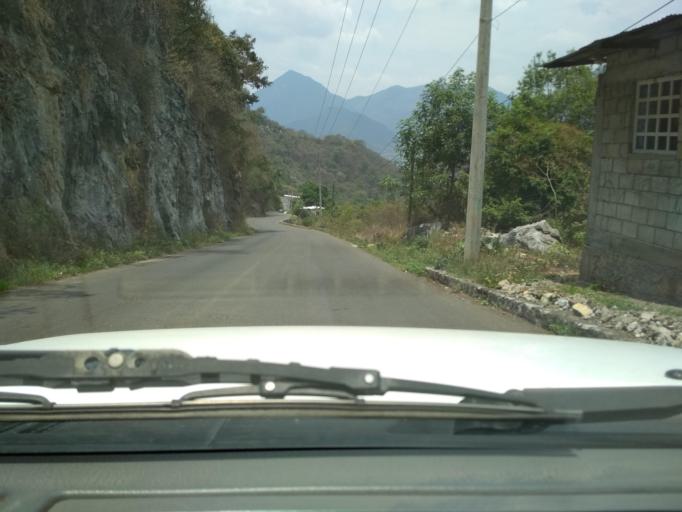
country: MX
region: Veracruz
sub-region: Camerino Z. Mendoza
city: La Cuesta
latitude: 18.7948
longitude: -97.1742
